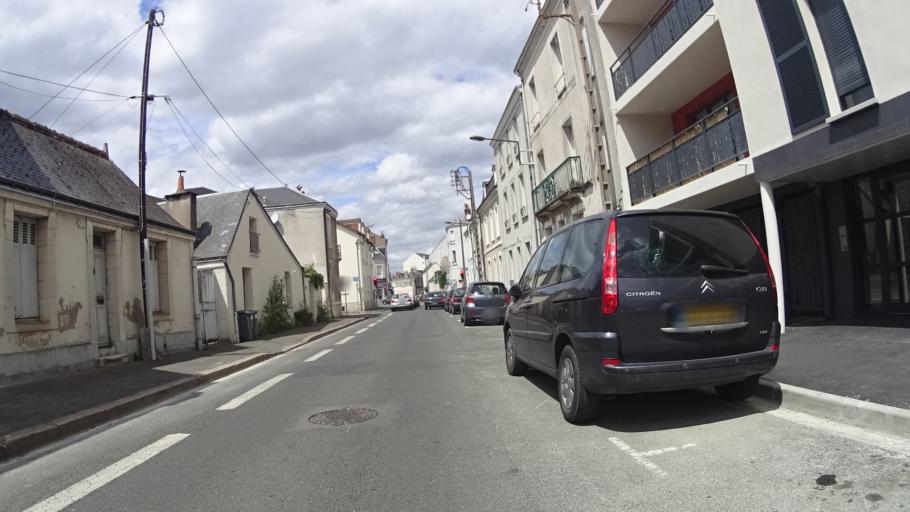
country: FR
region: Centre
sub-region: Departement d'Indre-et-Loire
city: Tours
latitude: 47.3817
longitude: 0.6790
